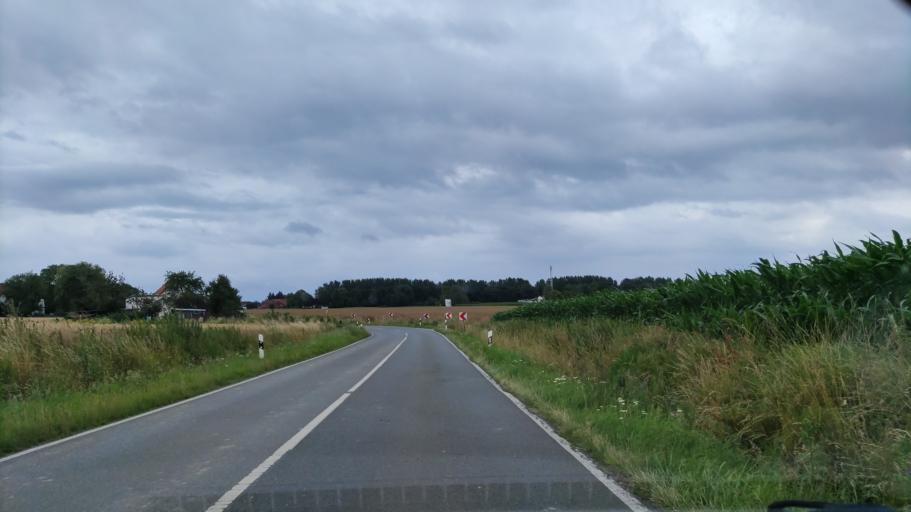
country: DE
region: North Rhine-Westphalia
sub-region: Regierungsbezirk Arnsberg
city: Soest
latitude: 51.6090
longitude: 8.0427
